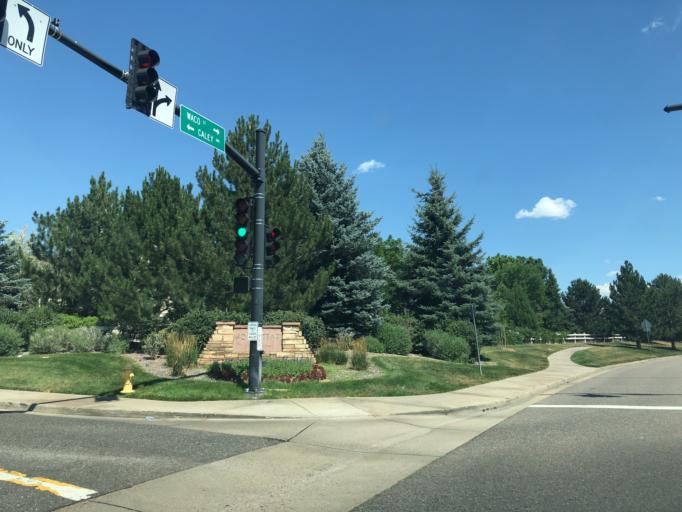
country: US
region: Colorado
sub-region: Arapahoe County
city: Dove Valley
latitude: 39.6023
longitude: -104.7823
